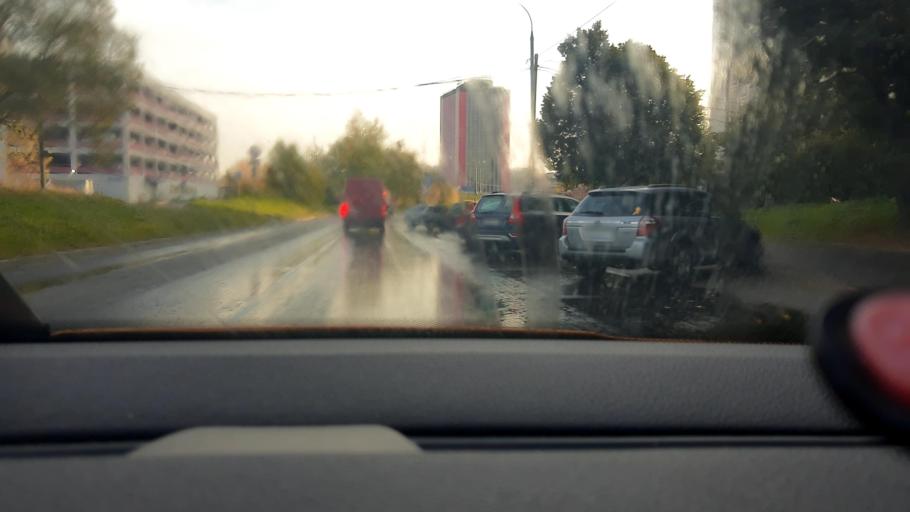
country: RU
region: Moscow
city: Gol'yanovo
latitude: 55.8160
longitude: 37.8353
